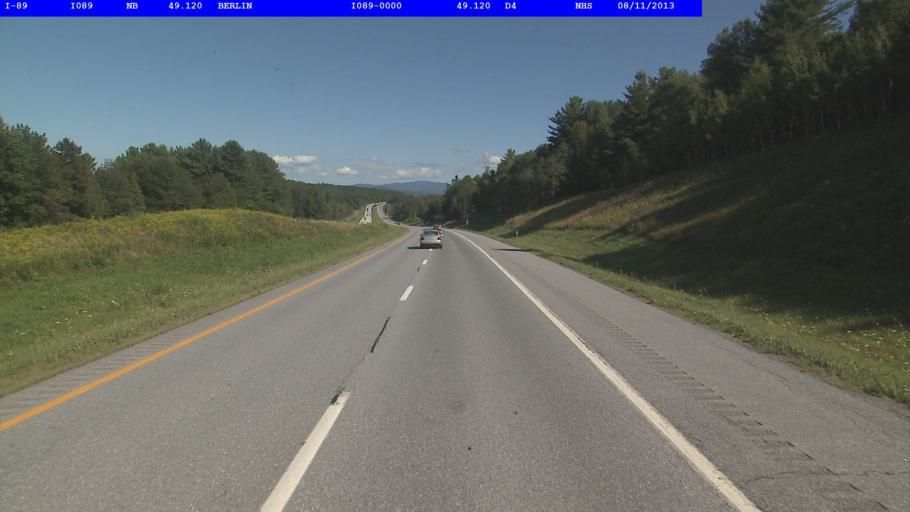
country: US
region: Vermont
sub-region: Washington County
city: Montpelier
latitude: 44.1993
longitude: -72.5771
